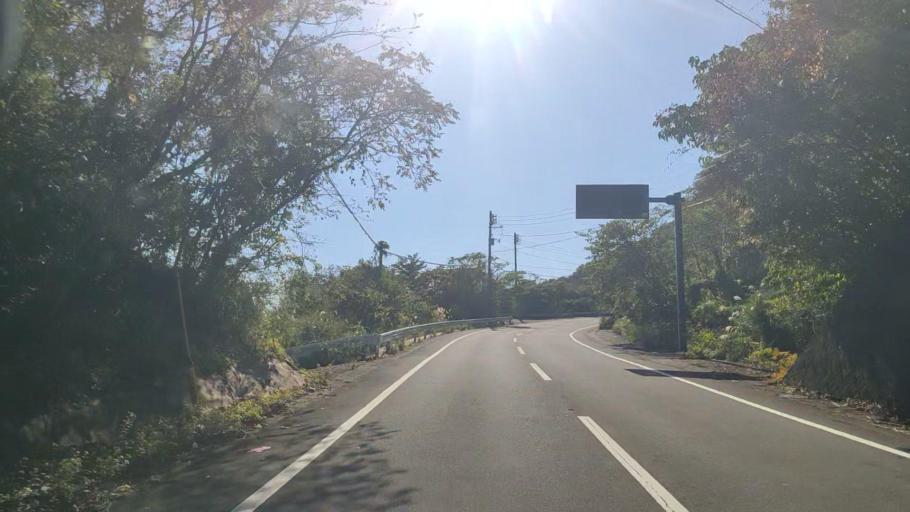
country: JP
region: Shizuoka
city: Atami
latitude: 35.0513
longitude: 139.0395
